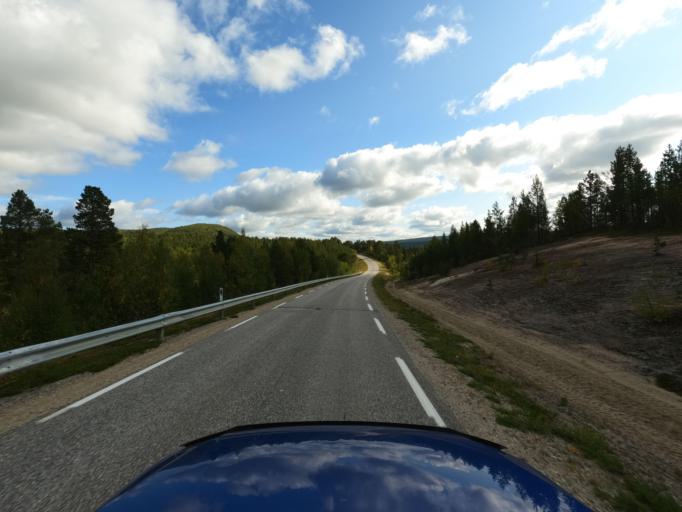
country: NO
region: Finnmark Fylke
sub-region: Karasjok
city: Karasjohka
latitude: 69.4431
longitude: 25.2679
